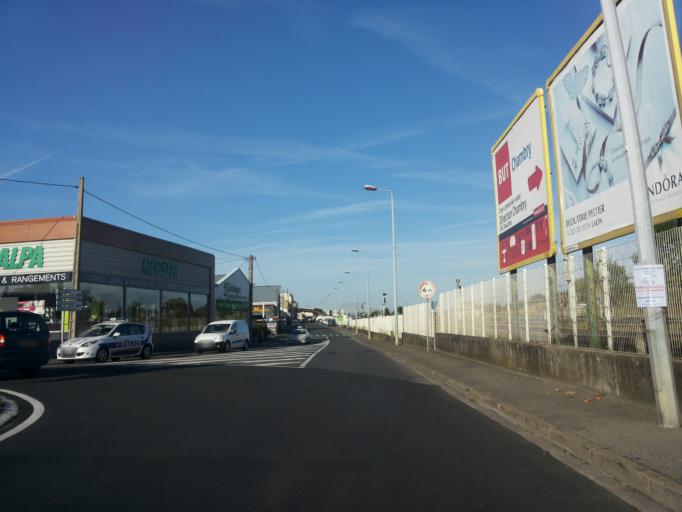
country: FR
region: Picardie
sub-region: Departement de l'Aisne
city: Laon
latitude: 49.5708
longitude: 3.6340
